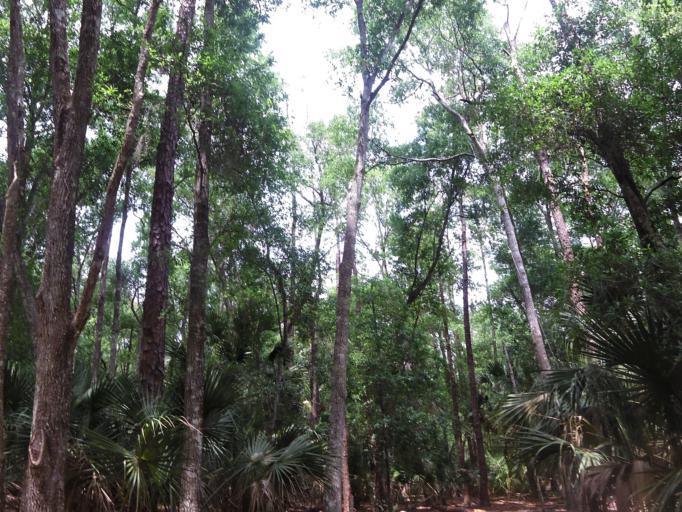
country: US
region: Florida
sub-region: Volusia County
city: Ormond-by-the-Sea
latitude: 29.3897
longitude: -81.1321
